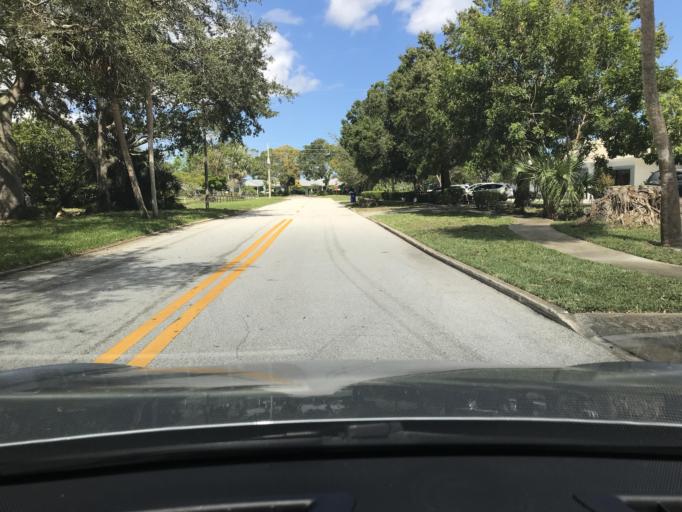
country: US
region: Florida
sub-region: Indian River County
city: Vero Beach
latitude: 27.6445
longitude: -80.4013
